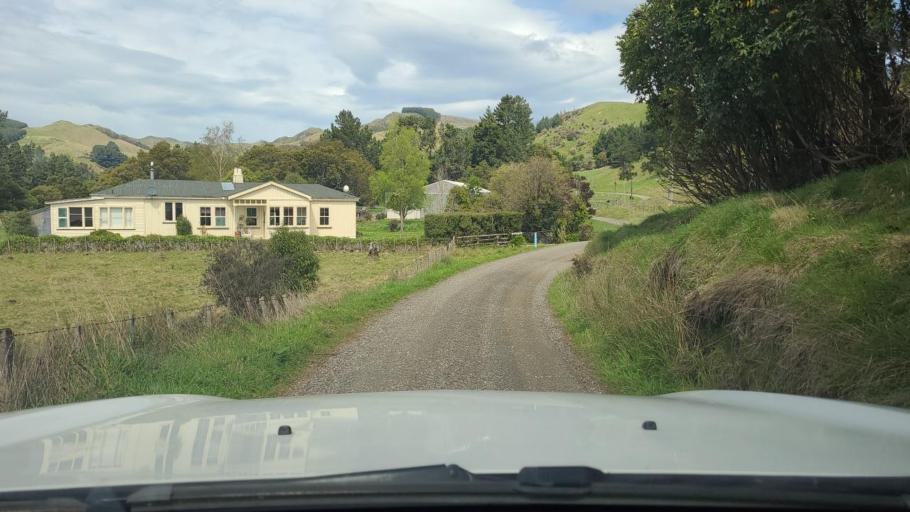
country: NZ
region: Wellington
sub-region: South Wairarapa District
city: Waipawa
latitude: -41.3421
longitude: 175.4135
